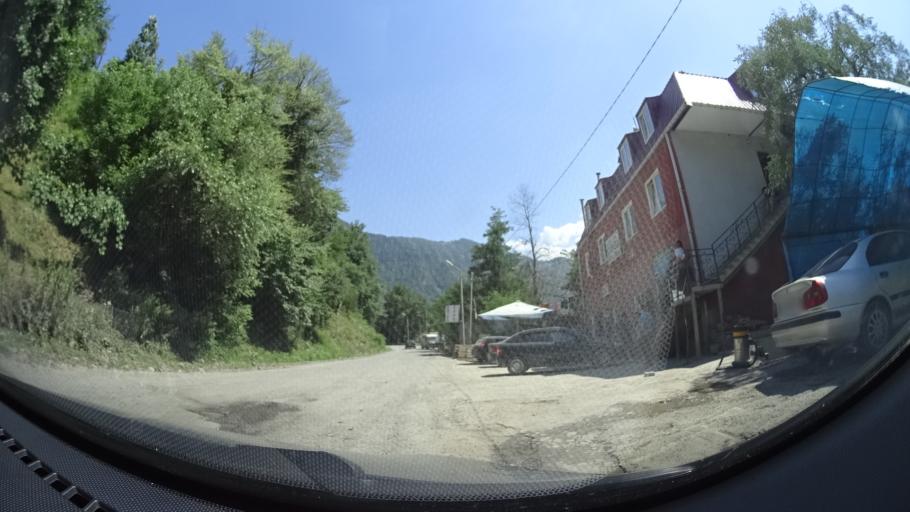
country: GE
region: Ajaria
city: Khulo
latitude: 41.6433
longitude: 42.3107
